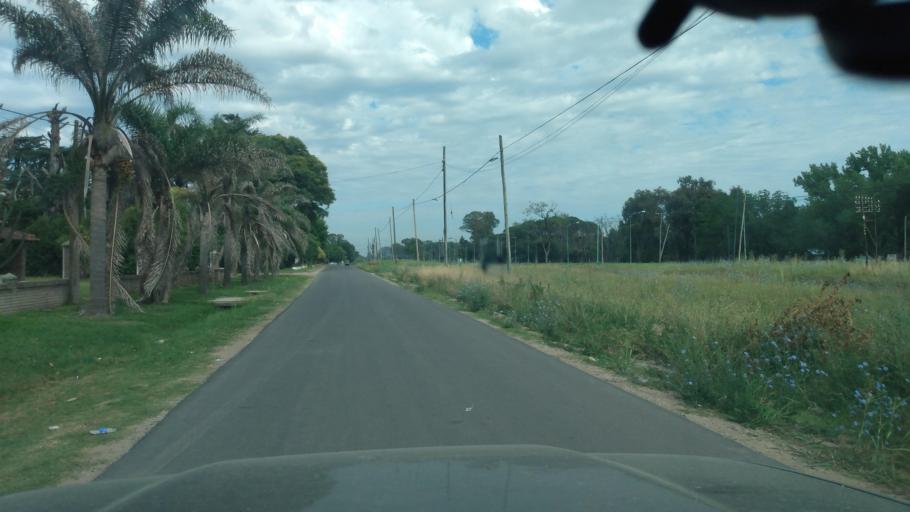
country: AR
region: Buenos Aires
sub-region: Partido de Lujan
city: Lujan
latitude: -34.5854
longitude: -59.0543
